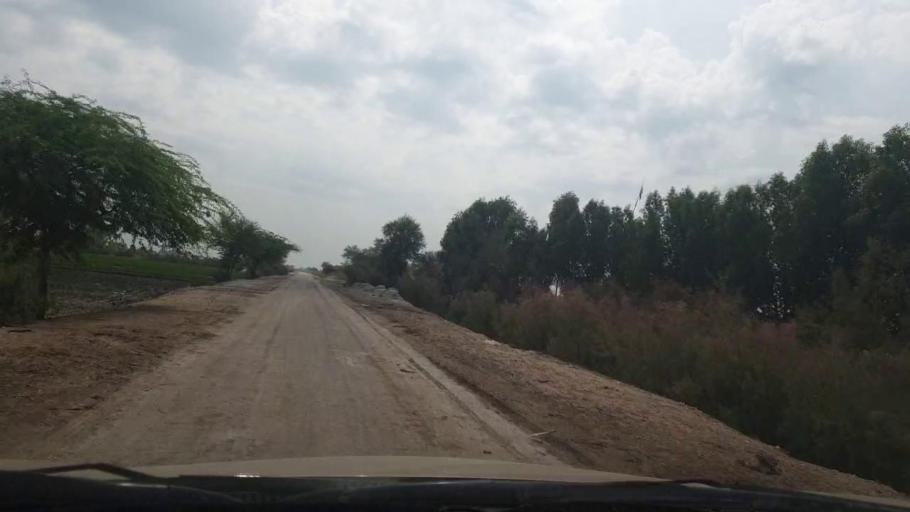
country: PK
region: Sindh
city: Miro Khan
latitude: 27.6967
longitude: 68.2069
